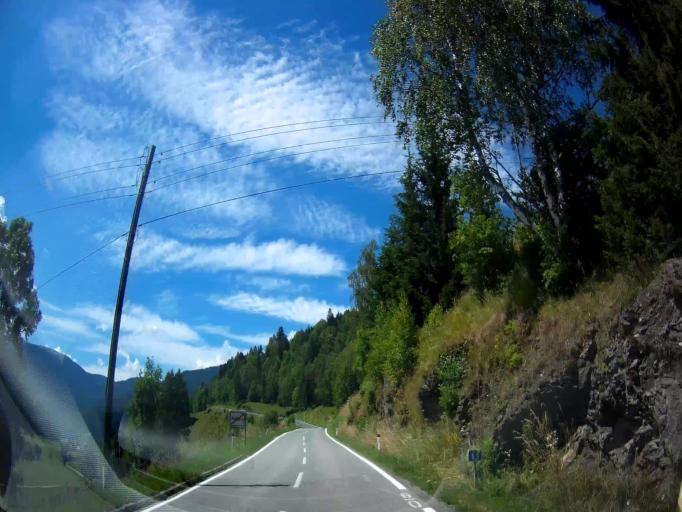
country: AT
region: Carinthia
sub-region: Politischer Bezirk Sankt Veit an der Glan
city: Glodnitz
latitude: 46.9007
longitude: 14.1068
